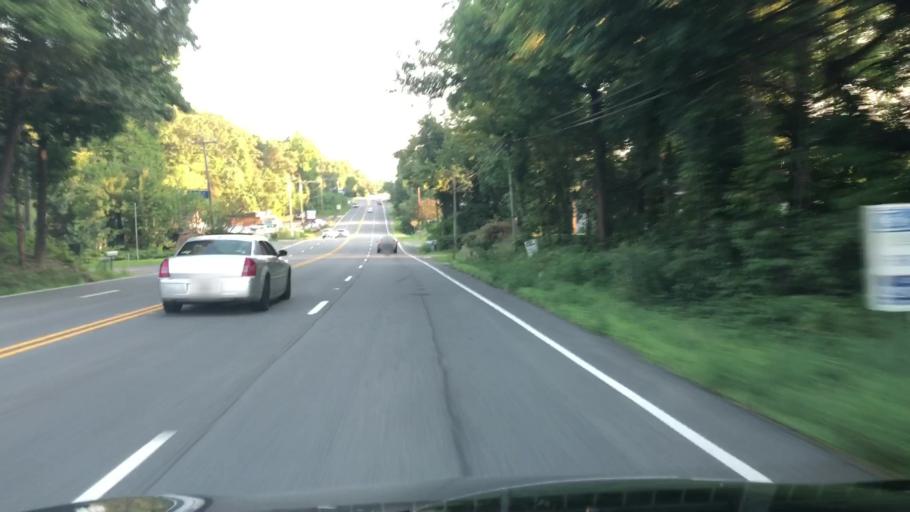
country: US
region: Virginia
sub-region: Stafford County
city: Falmouth
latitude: 38.3329
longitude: -77.4650
